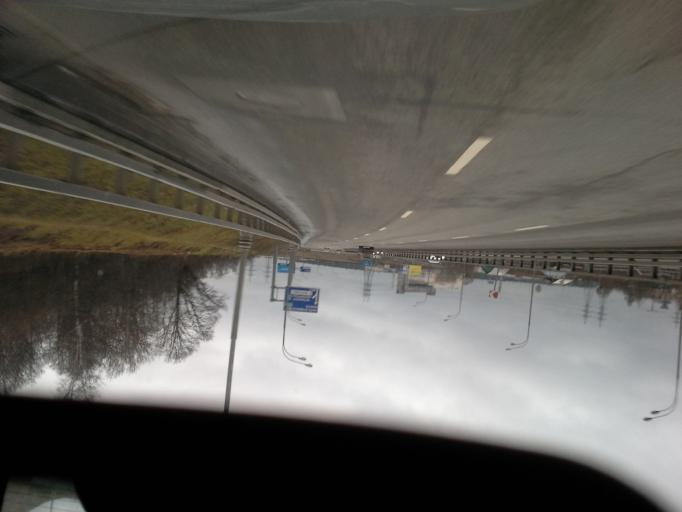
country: RU
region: Moskovskaya
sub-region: Leninskiy Rayon
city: Vnukovo
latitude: 55.6222
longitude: 37.2819
